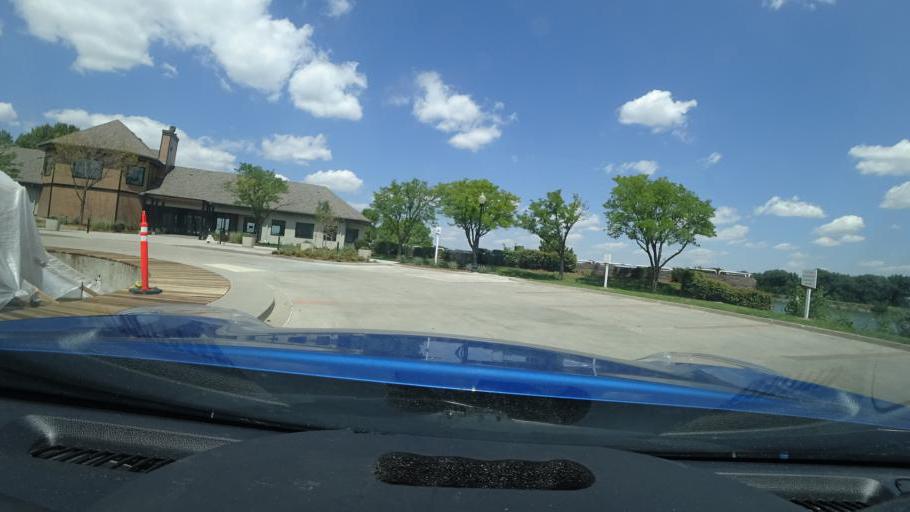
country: US
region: Colorado
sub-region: Arapahoe County
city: Glendale
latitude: 39.6988
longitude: -104.8824
